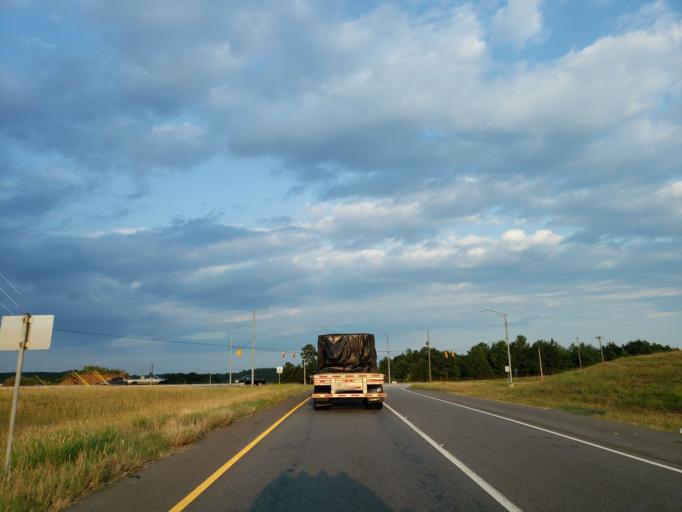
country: US
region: Alabama
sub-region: Tuscaloosa County
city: Holt
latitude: 33.1721
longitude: -87.4486
